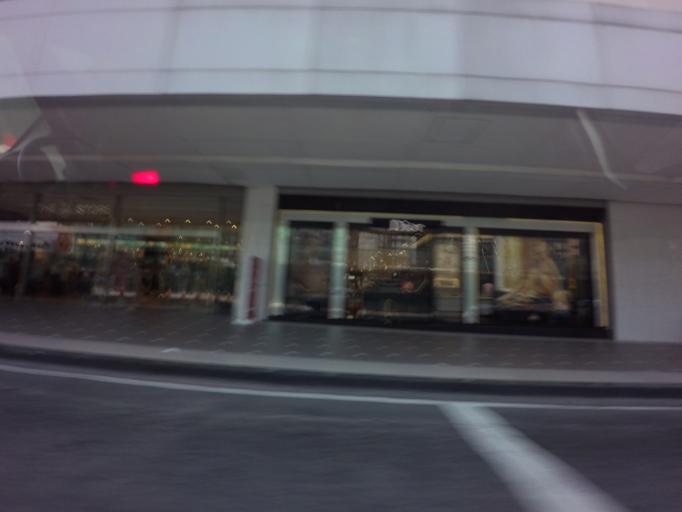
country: PH
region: Metro Manila
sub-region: Makati City
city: Makati City
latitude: 14.5502
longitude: 121.0270
